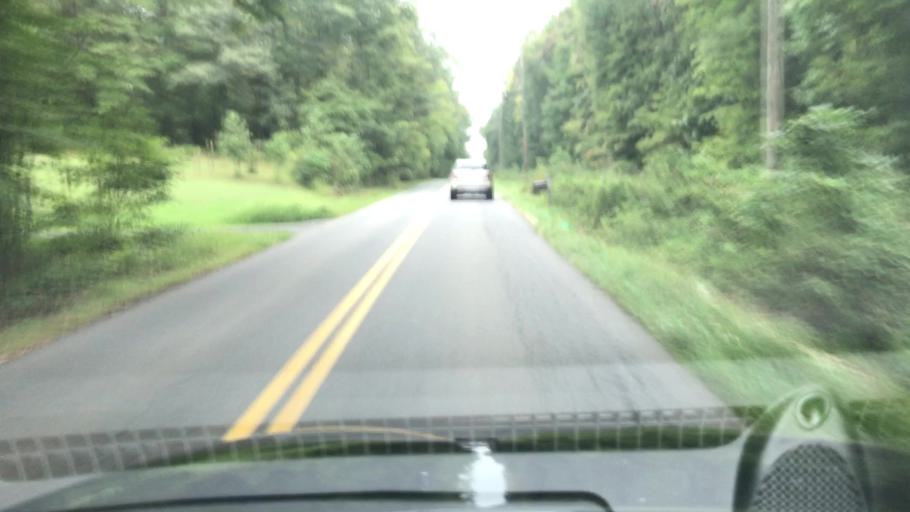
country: US
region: Virginia
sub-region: Fauquier County
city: New Baltimore
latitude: 38.7213
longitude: -77.6625
